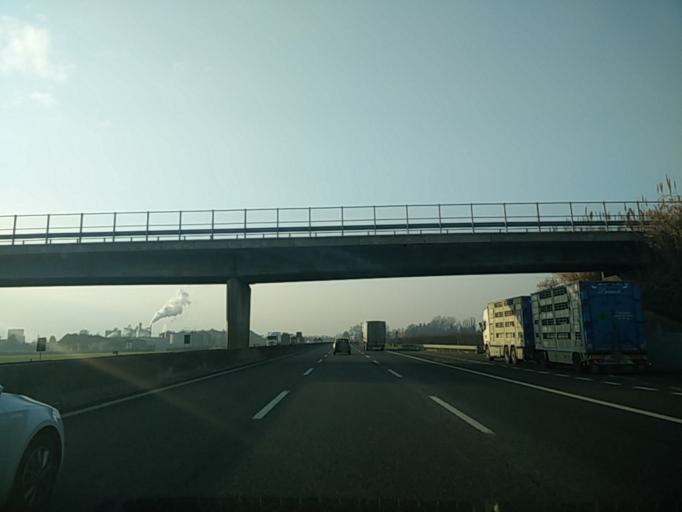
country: IT
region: Emilia-Romagna
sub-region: Provincia di Ravenna
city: Solarolo
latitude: 44.3354
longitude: 11.8761
